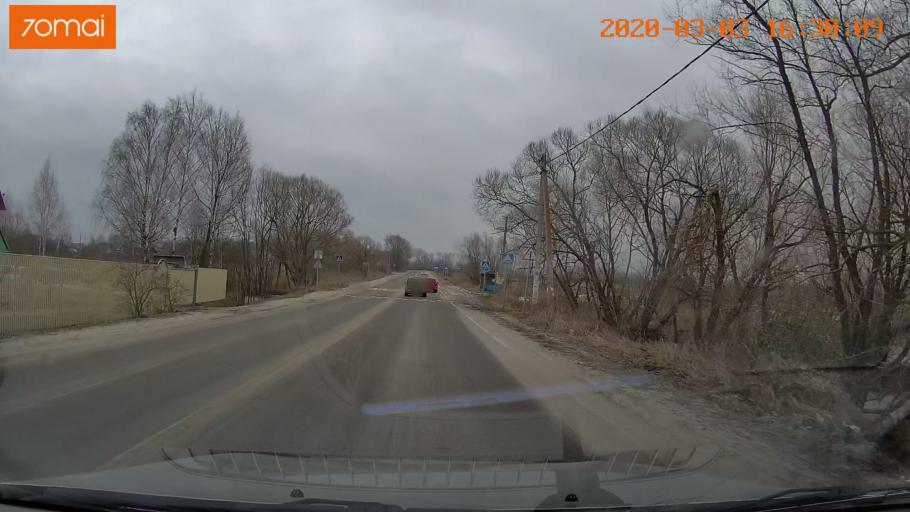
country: RU
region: Moskovskaya
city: Konobeyevo
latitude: 55.4342
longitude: 38.7090
